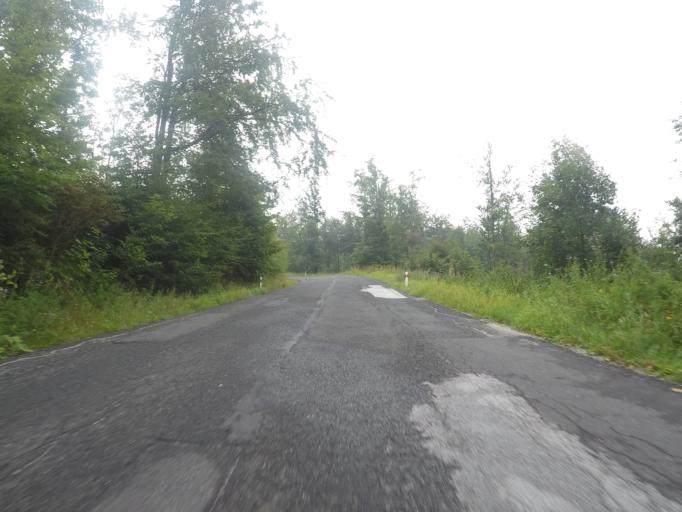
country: SK
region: Kosicky
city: Spisska Nova Ves
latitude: 48.8574
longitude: 20.5114
